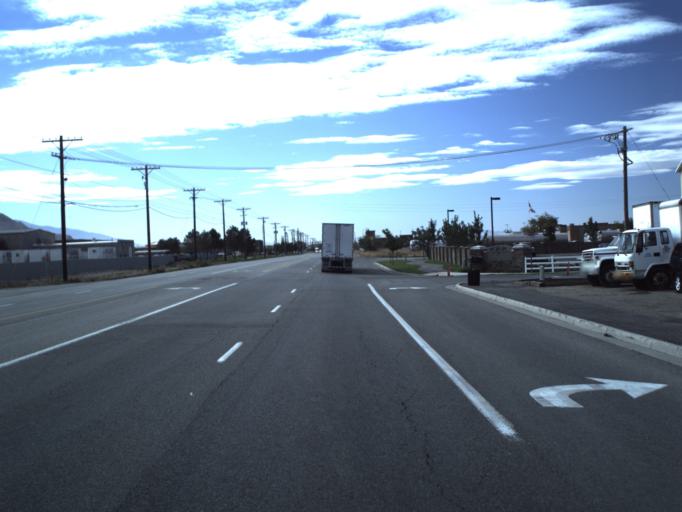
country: US
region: Utah
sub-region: Davis County
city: North Salt Lake
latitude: 40.8581
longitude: -111.9299
